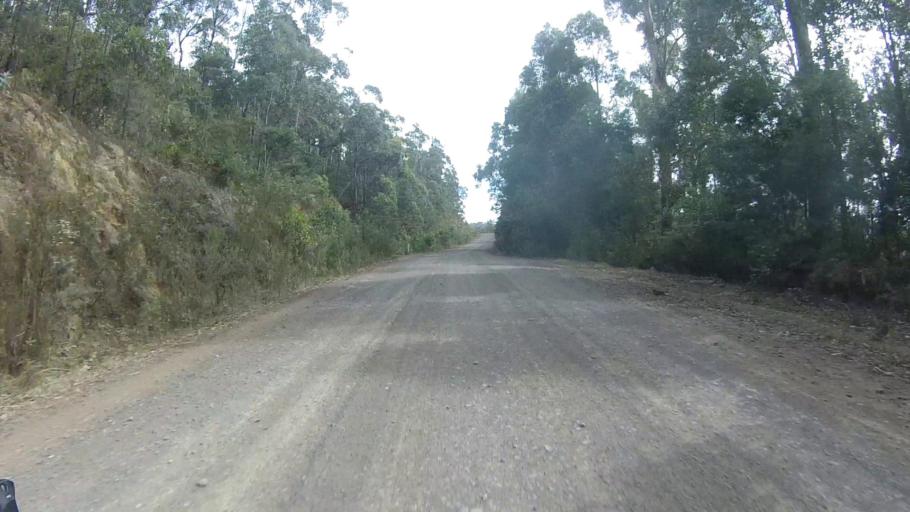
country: AU
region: Tasmania
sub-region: Sorell
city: Sorell
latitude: -42.7608
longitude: 147.8289
